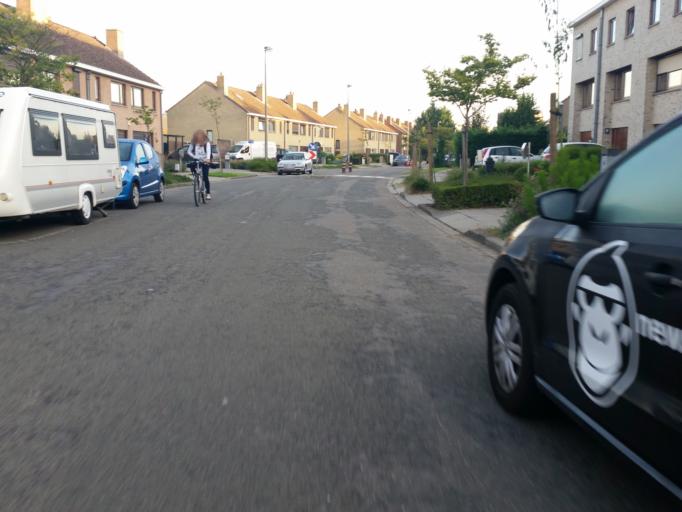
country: BE
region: Flanders
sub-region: Provincie Vlaams-Brabant
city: Vilvoorde
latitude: 50.9385
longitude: 4.4397
